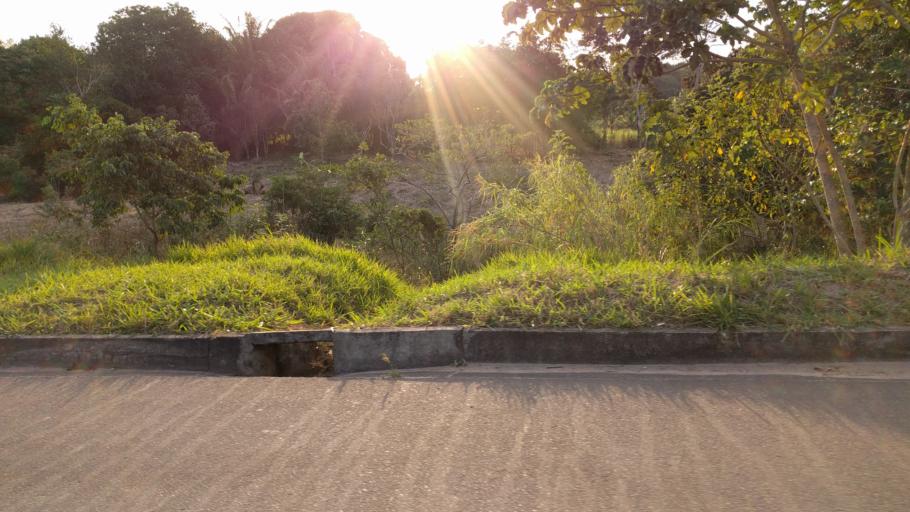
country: BO
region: Santa Cruz
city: Buena Vista
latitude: -17.4141
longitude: -63.6166
